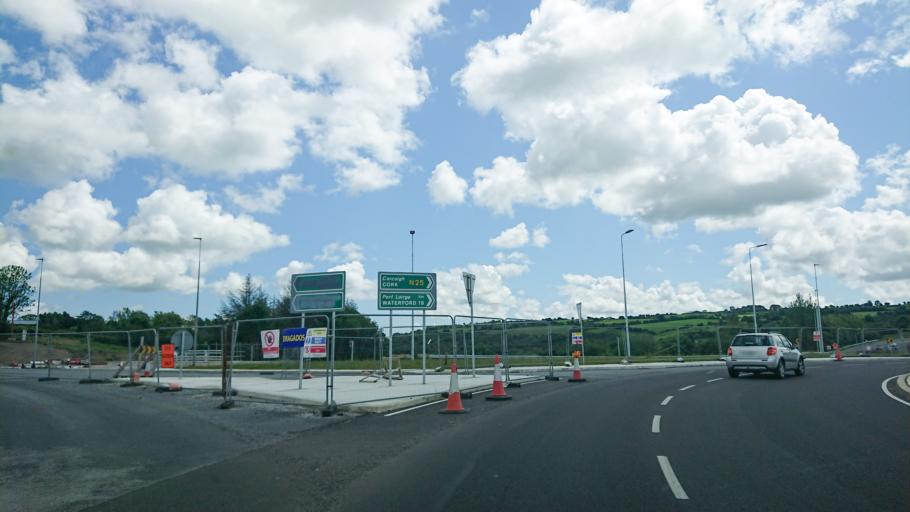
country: IE
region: Leinster
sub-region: Loch Garman
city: New Ross
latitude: 52.3611
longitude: -7.0129
